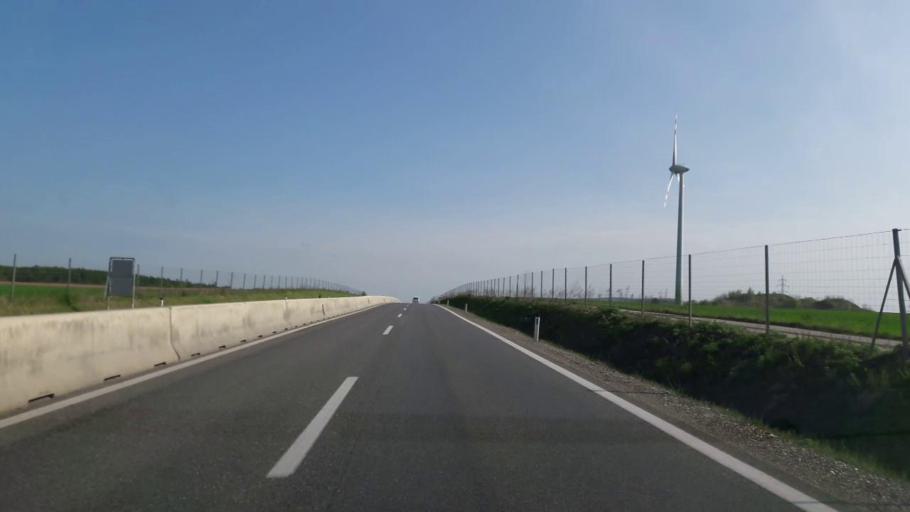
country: AT
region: Lower Austria
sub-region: Politischer Bezirk Hollabrunn
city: Hollabrunn
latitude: 48.5332
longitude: 16.0811
